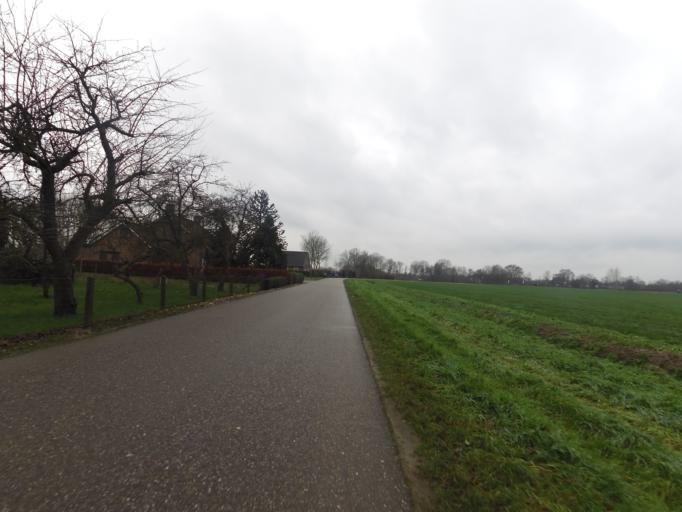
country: NL
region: Gelderland
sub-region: Gemeente Doetinchem
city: Doetinchem
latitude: 51.9605
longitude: 6.2278
